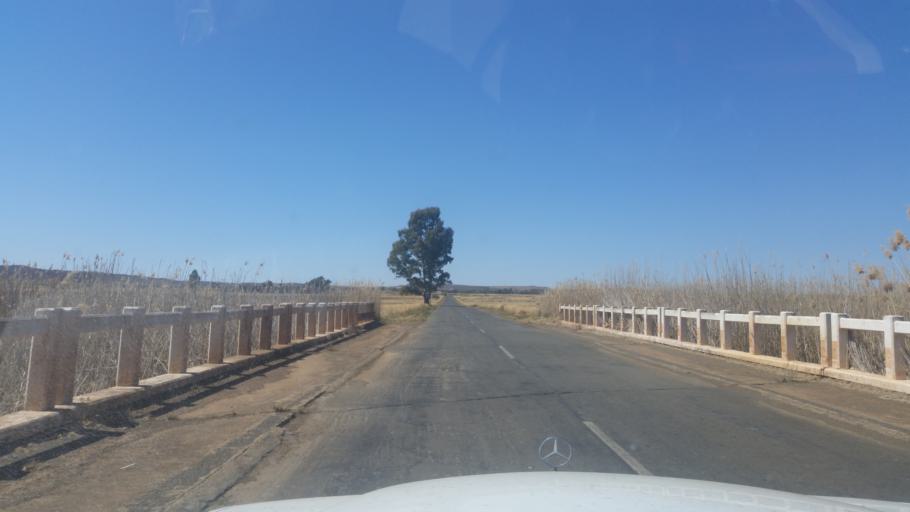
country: ZA
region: Eastern Cape
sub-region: Joe Gqabi District Municipality
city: Burgersdorp
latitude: -30.7575
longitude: 25.7774
